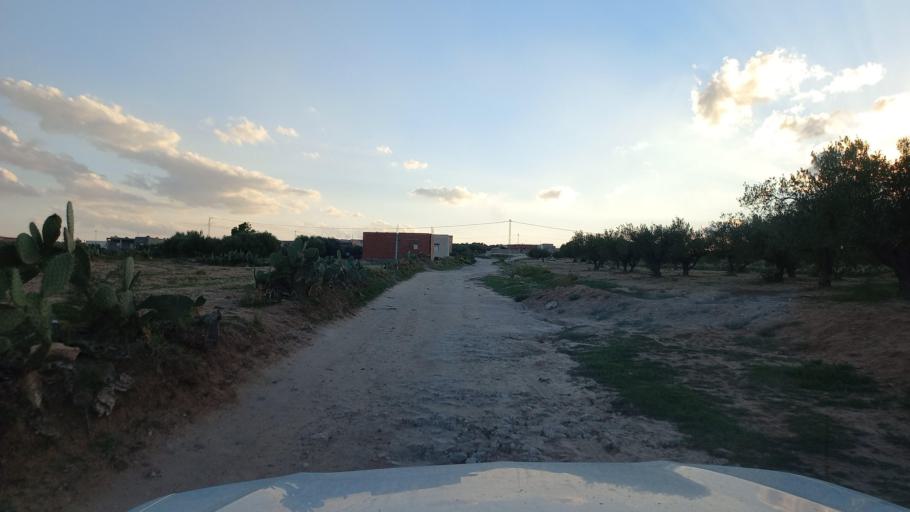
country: TN
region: Al Qasrayn
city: Sbiba
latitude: 35.3729
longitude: 9.0676
